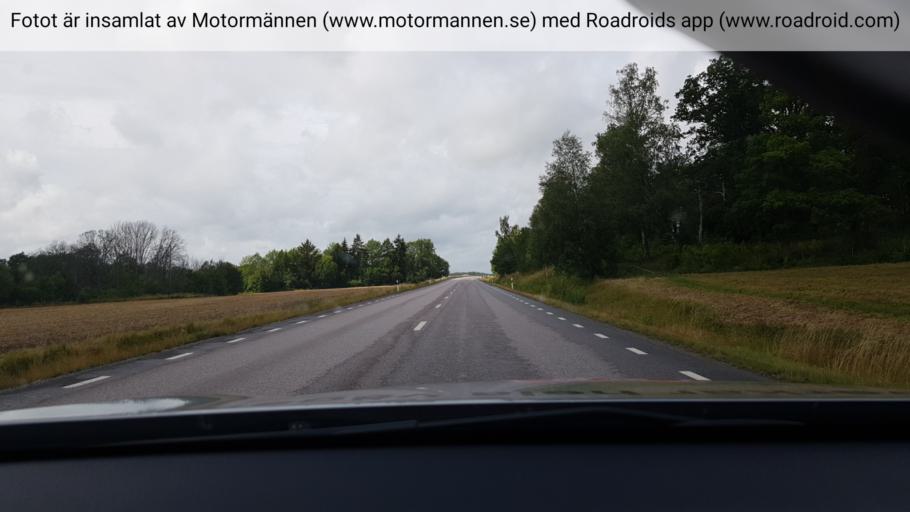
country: SE
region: Uppsala
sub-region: Osthammars Kommun
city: Bjorklinge
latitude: 59.9444
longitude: 17.4292
